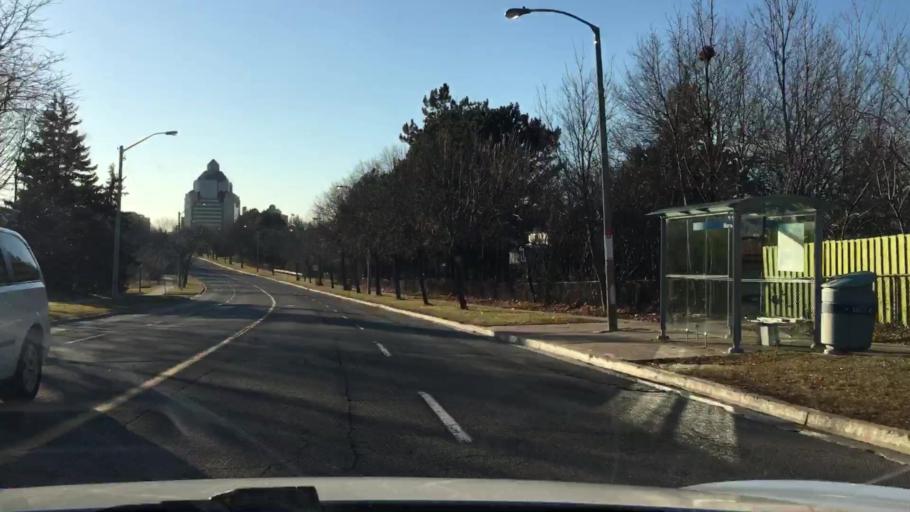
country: CA
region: Ontario
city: Scarborough
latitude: 43.7941
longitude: -79.2234
